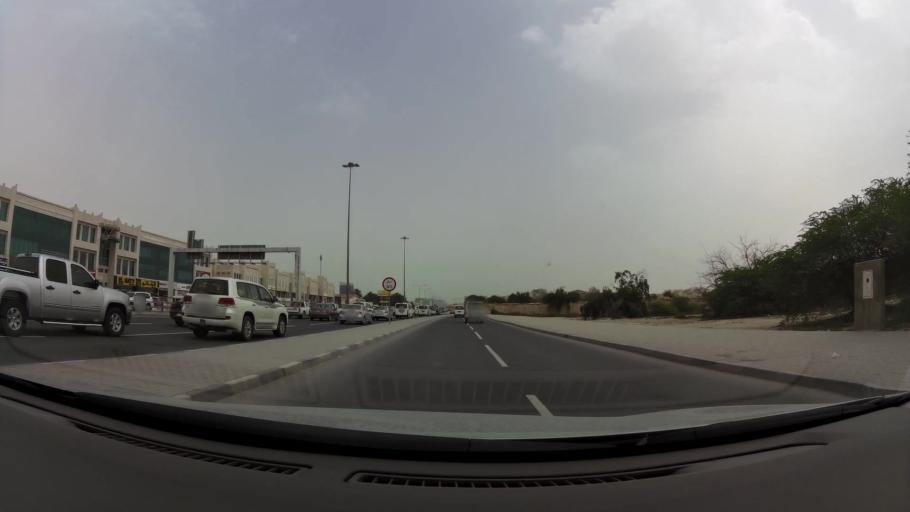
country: QA
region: Baladiyat ad Dawhah
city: Doha
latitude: 25.2661
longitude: 51.5008
